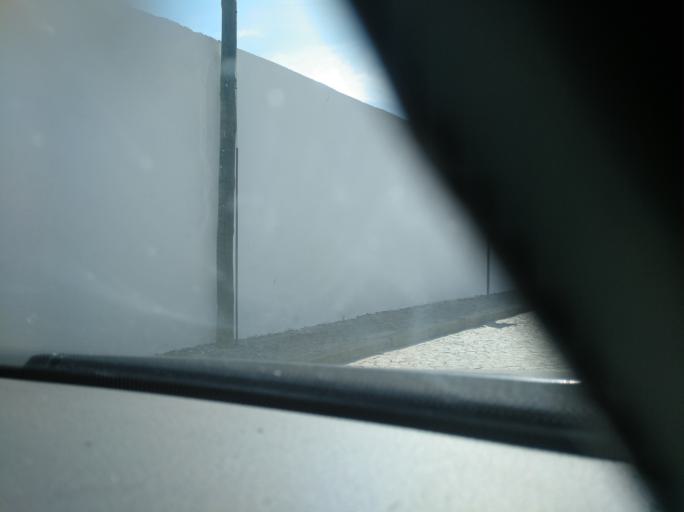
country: PT
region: Evora
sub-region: Vendas Novas
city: Vendas Novas
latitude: 38.6768
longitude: -8.4591
